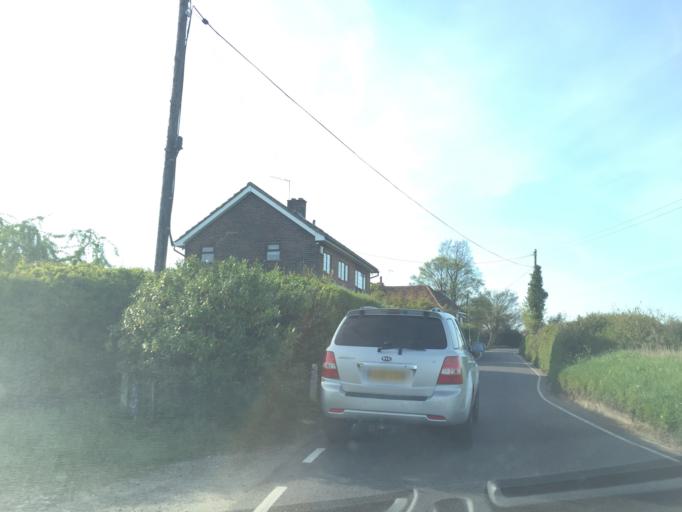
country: GB
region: England
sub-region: Essex
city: Harlow
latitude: 51.7387
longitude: 0.1005
